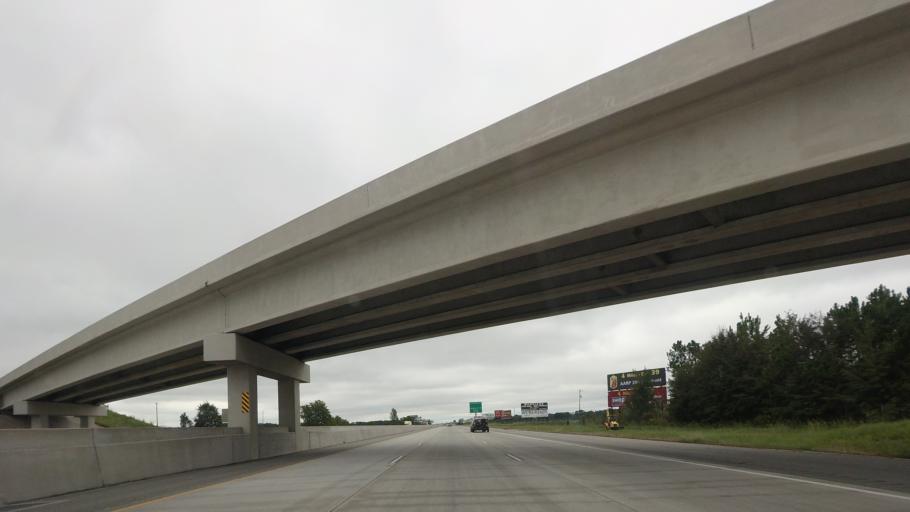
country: US
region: Georgia
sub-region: Cook County
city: Sparks
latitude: 31.1853
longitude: -83.4539
